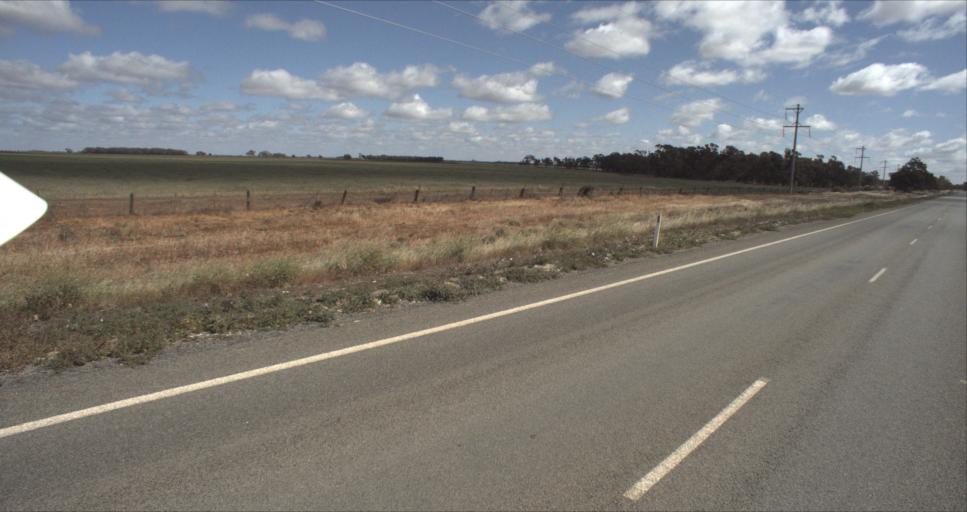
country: AU
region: New South Wales
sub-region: Murrumbidgee Shire
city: Darlington Point
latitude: -34.5792
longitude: 146.1654
